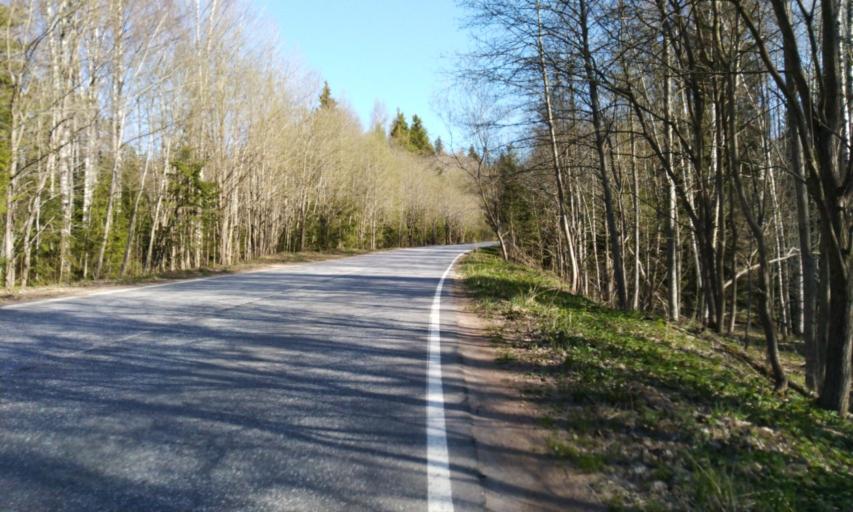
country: RU
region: Leningrad
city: Garbolovo
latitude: 60.3685
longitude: 30.4406
